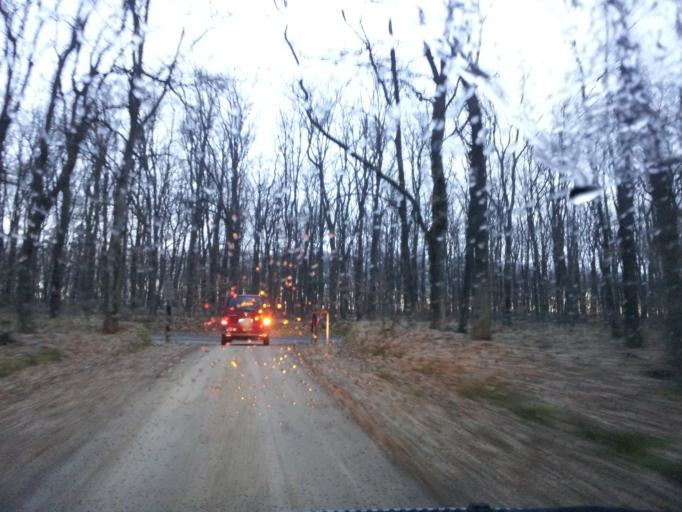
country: HU
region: Vas
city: Koszeg
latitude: 47.3965
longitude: 16.5939
